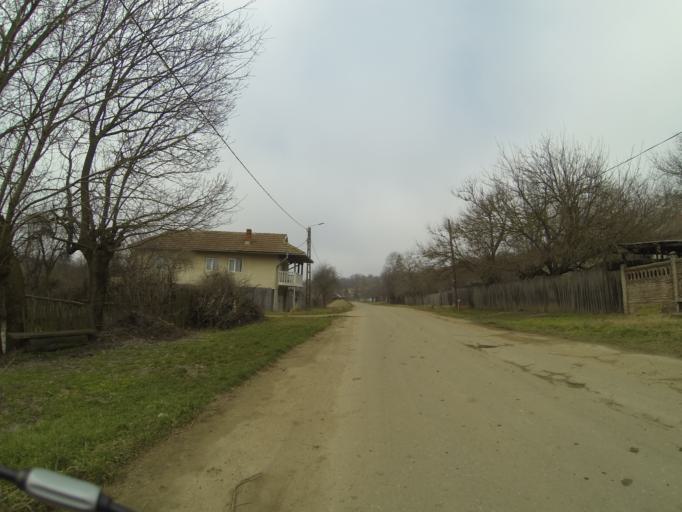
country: RO
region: Mehedinti
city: Padina Mica
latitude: 44.4908
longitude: 23.0088
